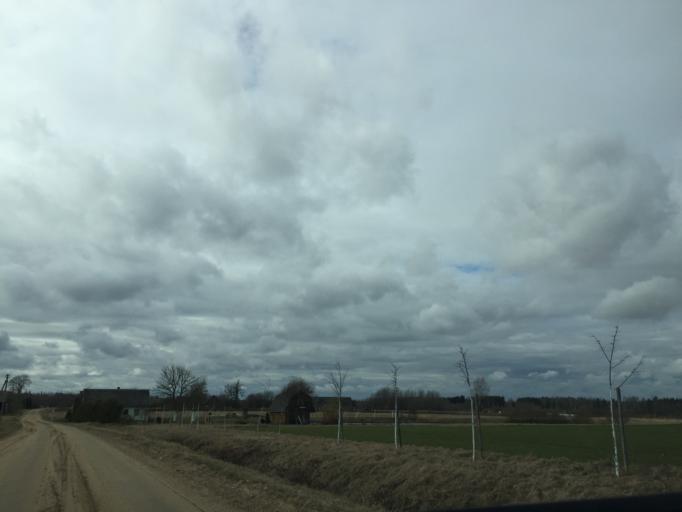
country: LV
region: Daugavpils
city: Daugavpils
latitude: 55.9481
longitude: 26.7031
